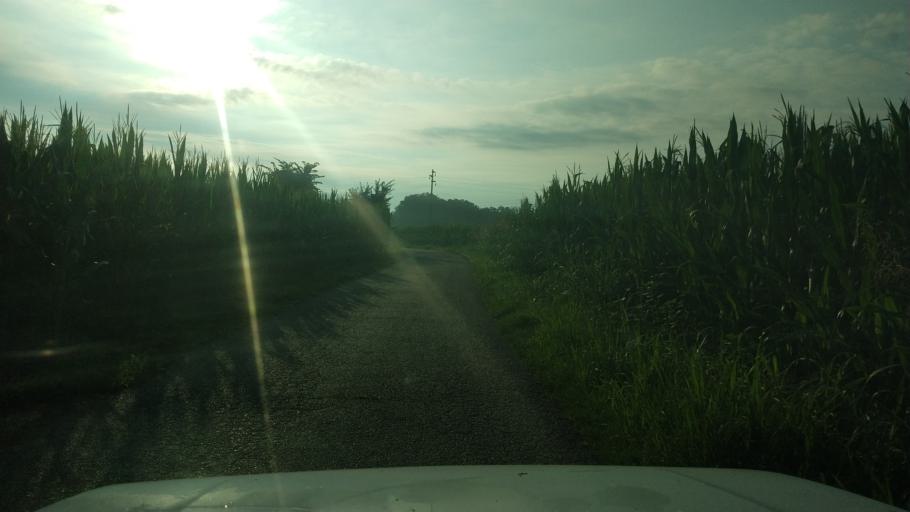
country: IT
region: Veneto
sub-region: Provincia di Vicenza
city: Nove
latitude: 45.7221
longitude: 11.6612
